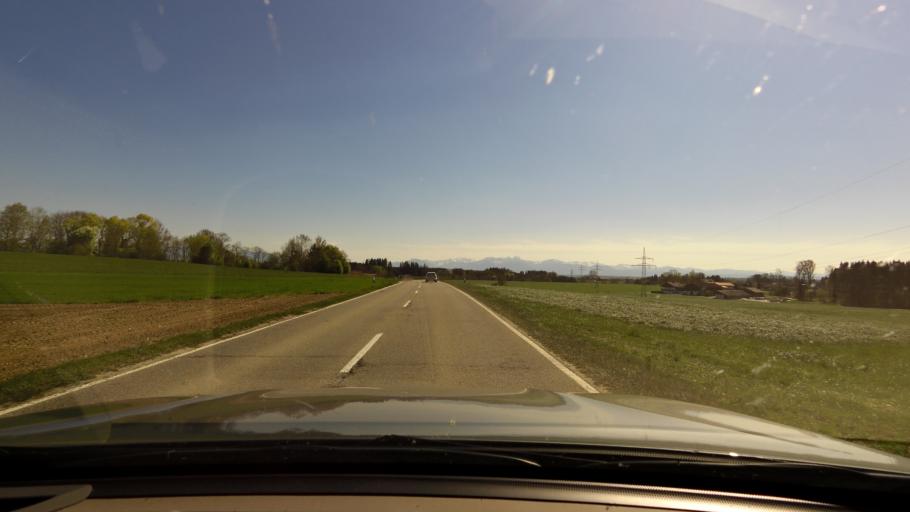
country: DE
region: Bavaria
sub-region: Upper Bavaria
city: Griesstatt
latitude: 47.9730
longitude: 12.1754
